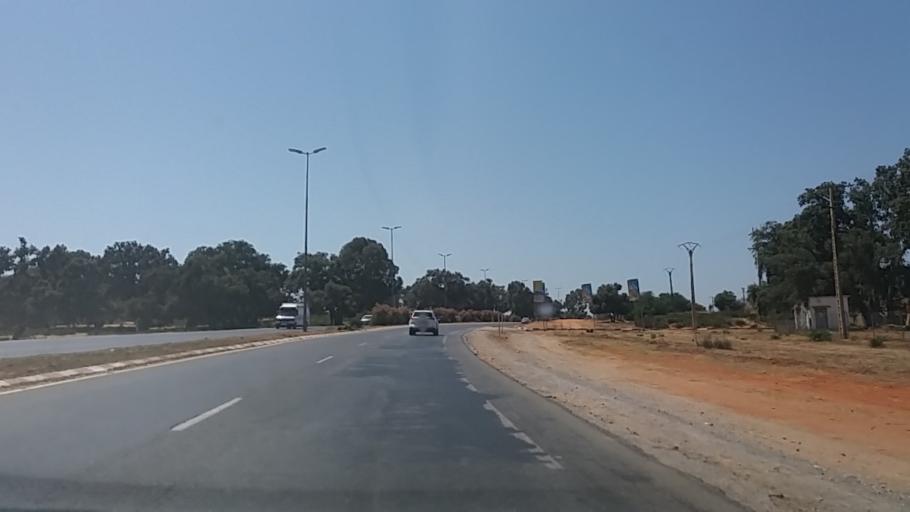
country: MA
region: Rabat-Sale-Zemmour-Zaer
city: Sale
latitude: 34.0248
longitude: -6.7201
